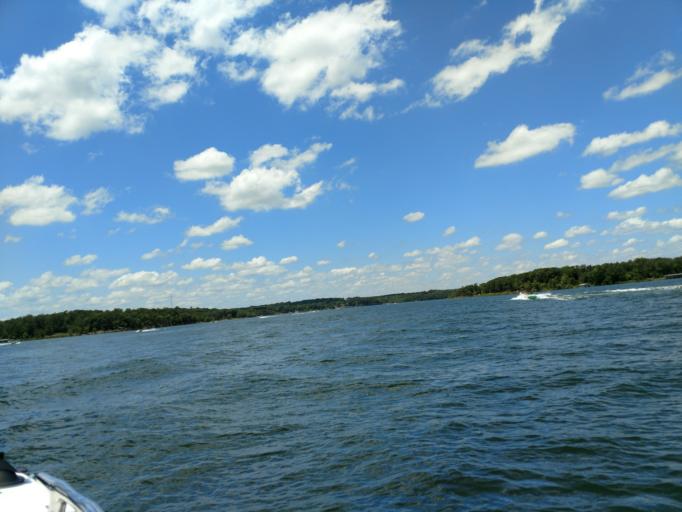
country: US
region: Missouri
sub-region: Barry County
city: Shell Knob
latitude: 36.5887
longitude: -93.5616
